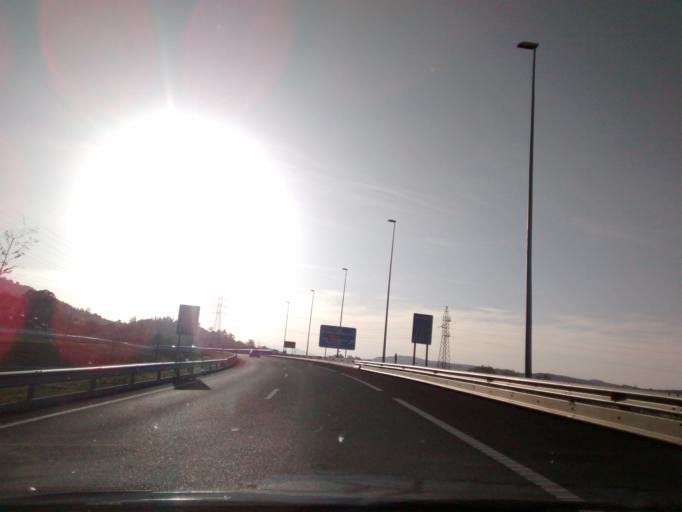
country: ES
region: Cantabria
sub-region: Provincia de Cantabria
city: El Astillero
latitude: 43.3947
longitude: -3.8054
